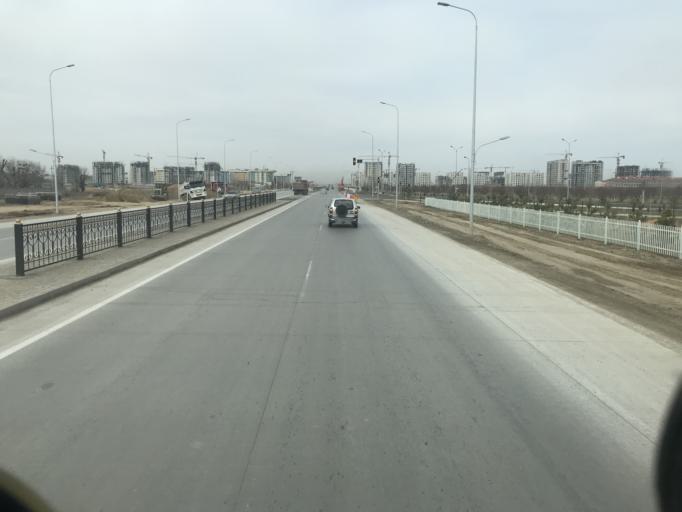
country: KZ
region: Ongtustik Qazaqstan
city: Turkestan
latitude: 43.2672
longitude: 68.3589
